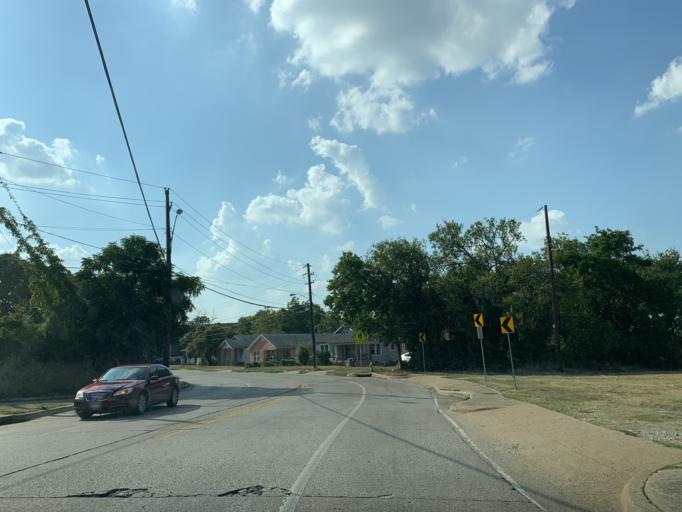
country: US
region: Texas
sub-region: Dallas County
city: Dallas
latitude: 32.7510
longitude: -96.8038
